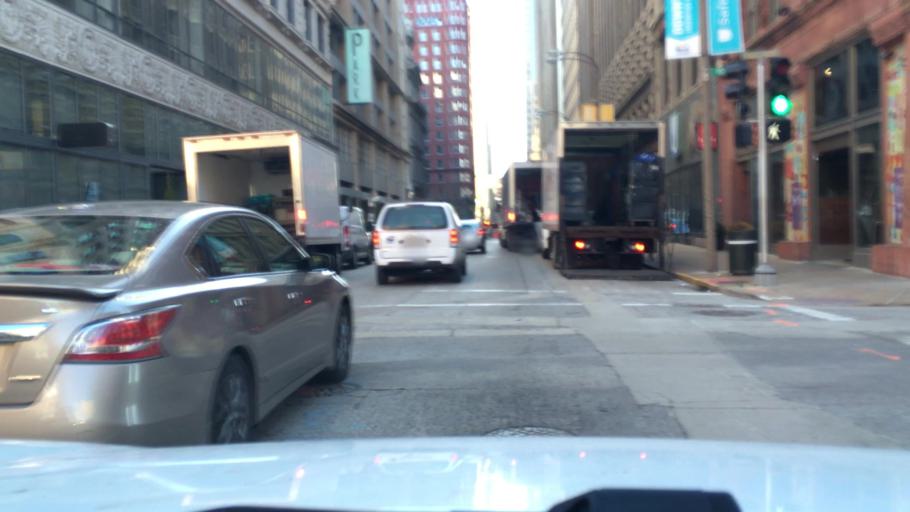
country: US
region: Missouri
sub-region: City of Saint Louis
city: St. Louis
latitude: 38.6291
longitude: -90.1948
